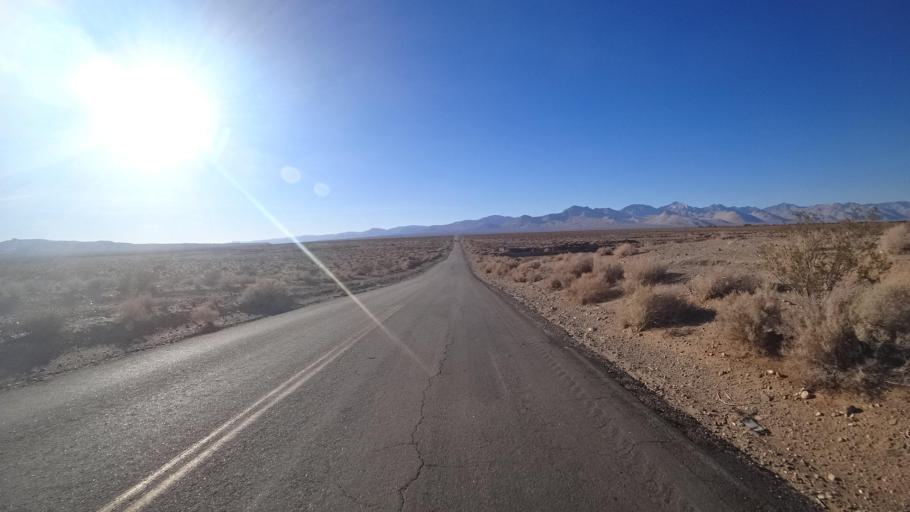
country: US
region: California
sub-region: Kern County
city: China Lake Acres
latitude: 35.6077
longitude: -117.7476
